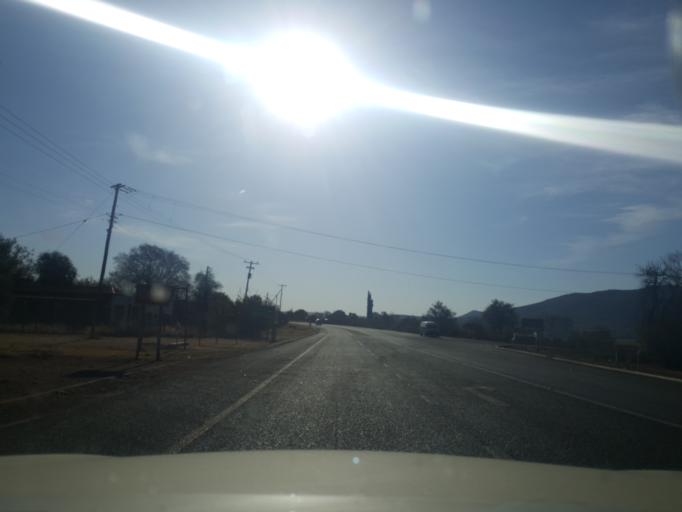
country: ZA
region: North-West
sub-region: Ngaka Modiri Molema District Municipality
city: Zeerust
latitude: -25.4484
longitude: 25.8652
